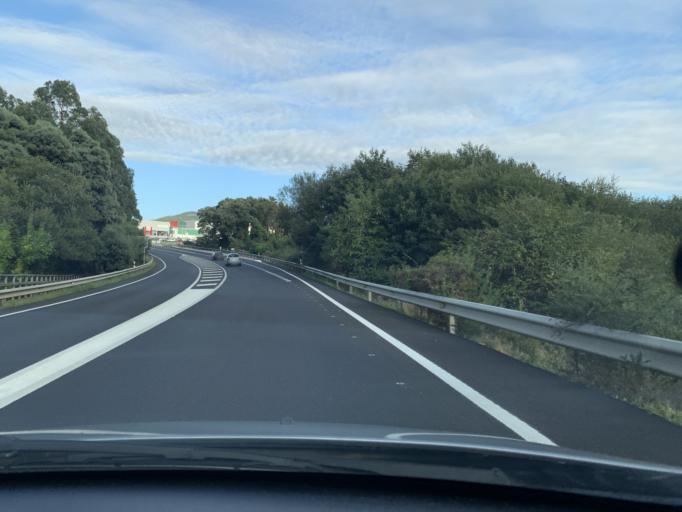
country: ES
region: Galicia
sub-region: Provincia de Lugo
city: Foz
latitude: 43.5403
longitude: -7.2674
